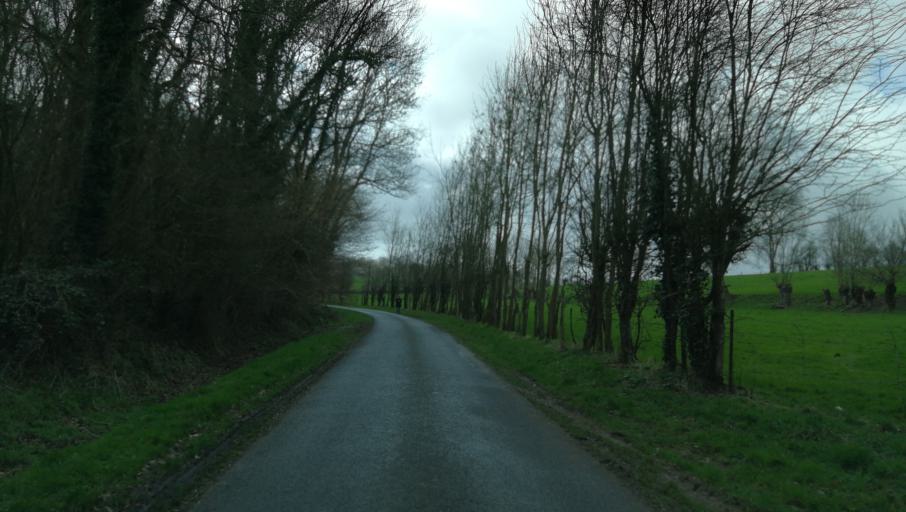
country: FR
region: Haute-Normandie
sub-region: Departement de l'Eure
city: Lieurey
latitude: 49.2312
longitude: 0.5434
